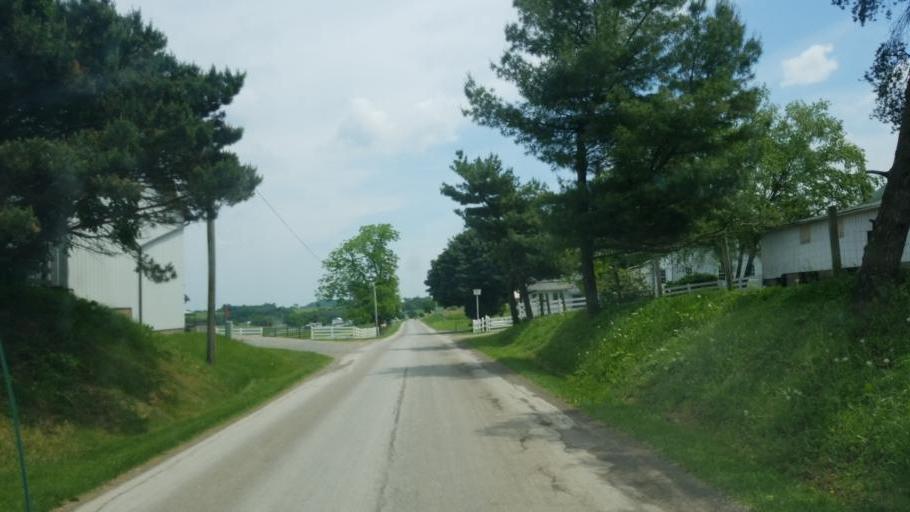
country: US
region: Ohio
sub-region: Tuscarawas County
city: Sugarcreek
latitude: 40.4586
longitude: -81.7836
